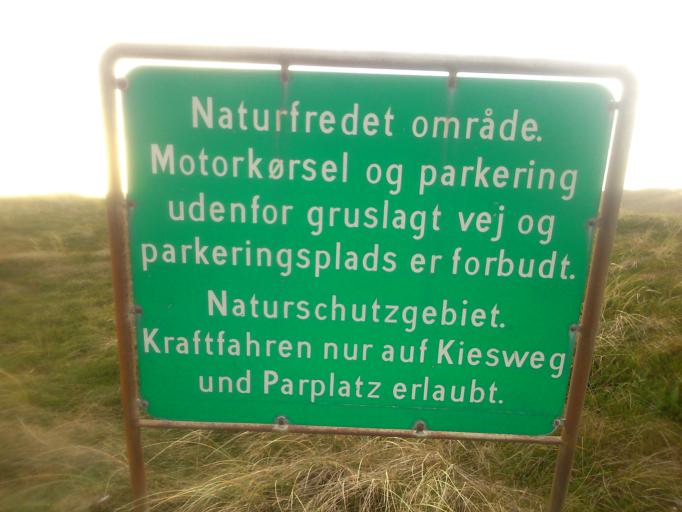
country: DK
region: Central Jutland
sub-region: Ringkobing-Skjern Kommune
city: Hvide Sande
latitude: 55.8165
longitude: 8.1774
